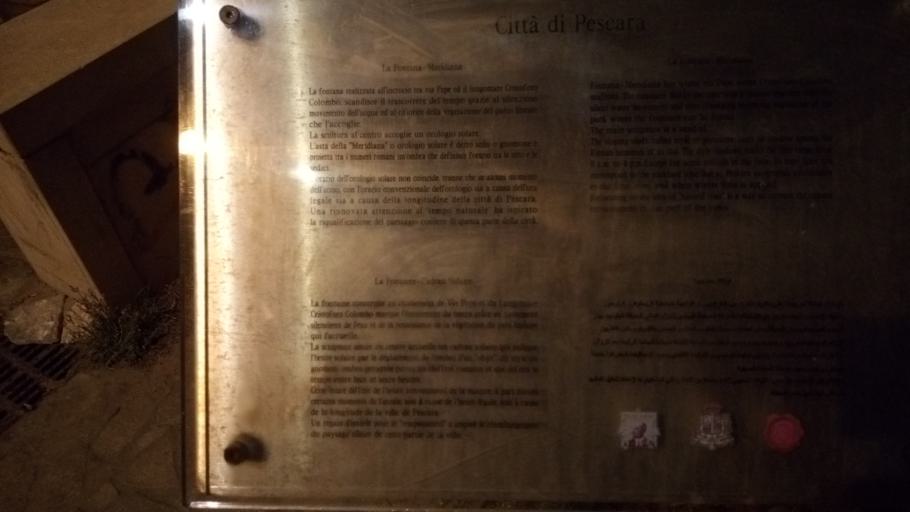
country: IT
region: Abruzzo
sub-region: Provincia di Pescara
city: Pescara
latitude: 42.4595
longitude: 14.2331
